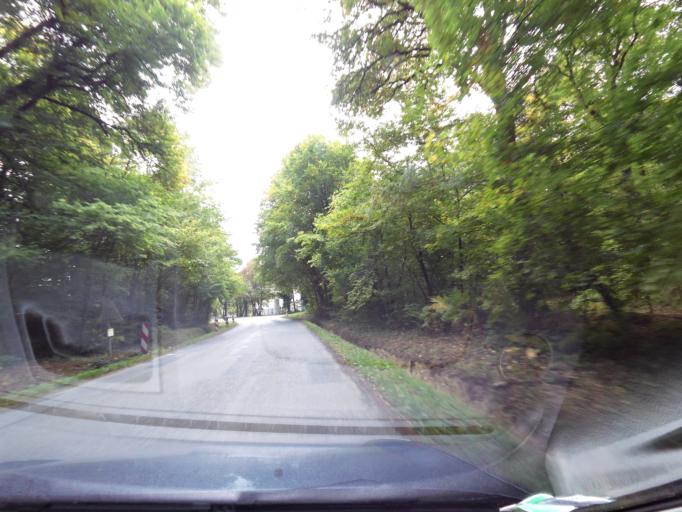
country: FR
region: Brittany
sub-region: Departement d'Ille-et-Vilaine
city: Vern-sur-Seiche
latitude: 48.0630
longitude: -1.6035
